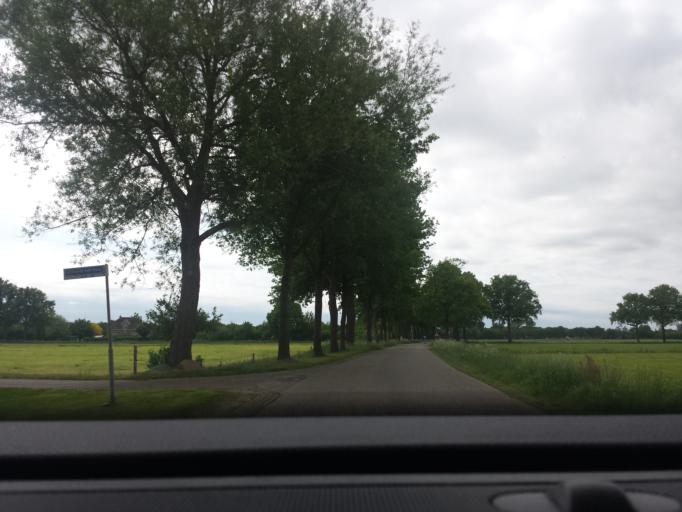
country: NL
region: Gelderland
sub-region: Oost Gelre
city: Lichtenvoorde
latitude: 52.0330
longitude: 6.5899
